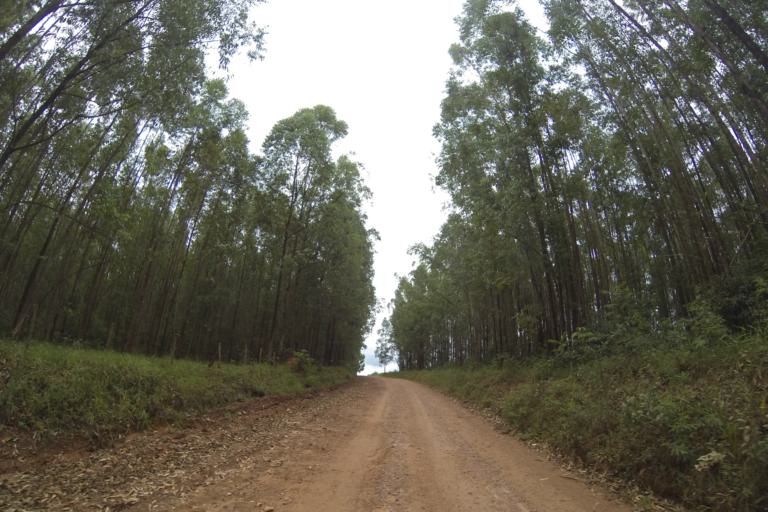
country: BR
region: Minas Gerais
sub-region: Ibia
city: Ibia
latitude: -19.6645
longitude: -46.6979
